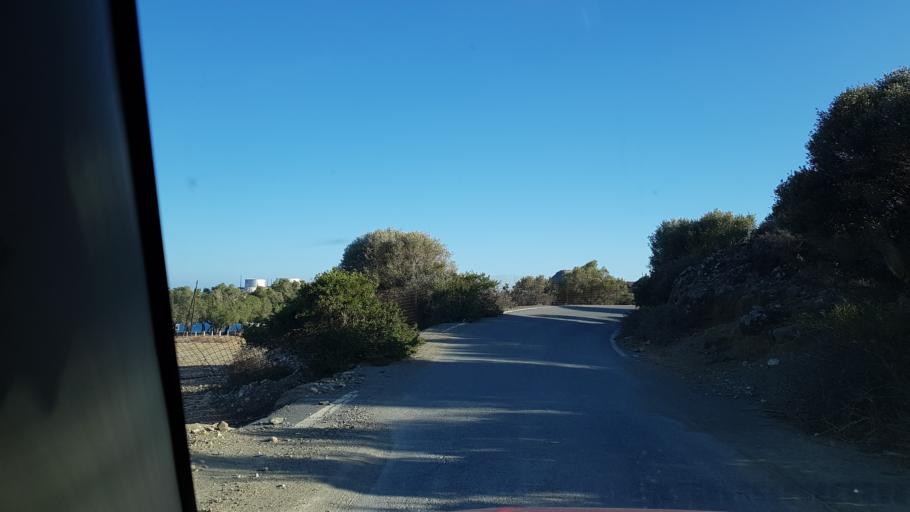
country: GR
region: Crete
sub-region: Nomos Irakleiou
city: Moires
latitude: 34.9357
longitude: 24.8054
